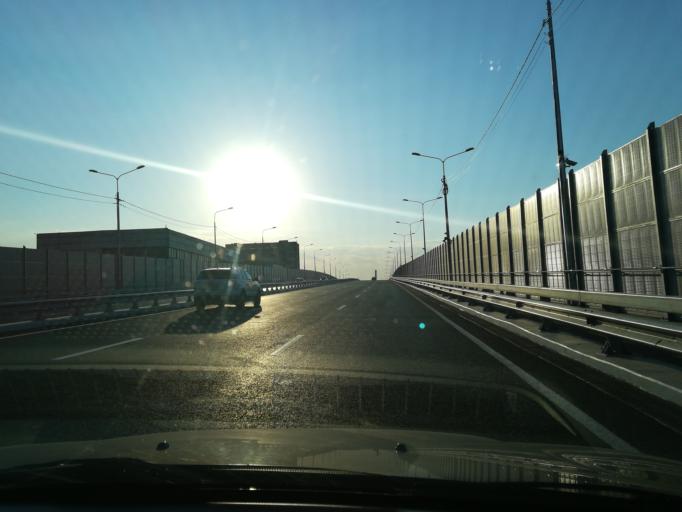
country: RU
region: Leningrad
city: Krestovskiy ostrov
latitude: 59.9556
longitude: 30.2617
